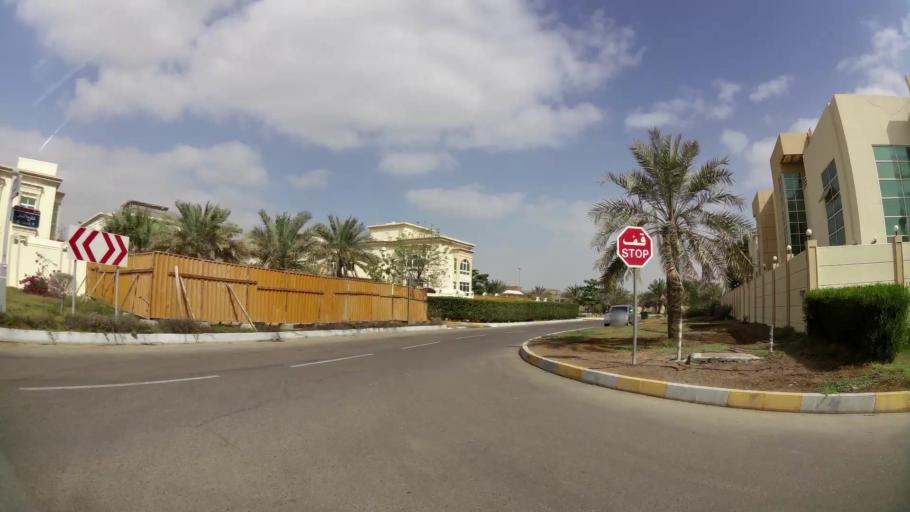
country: AE
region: Abu Dhabi
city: Abu Dhabi
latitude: 24.4105
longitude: 54.4934
